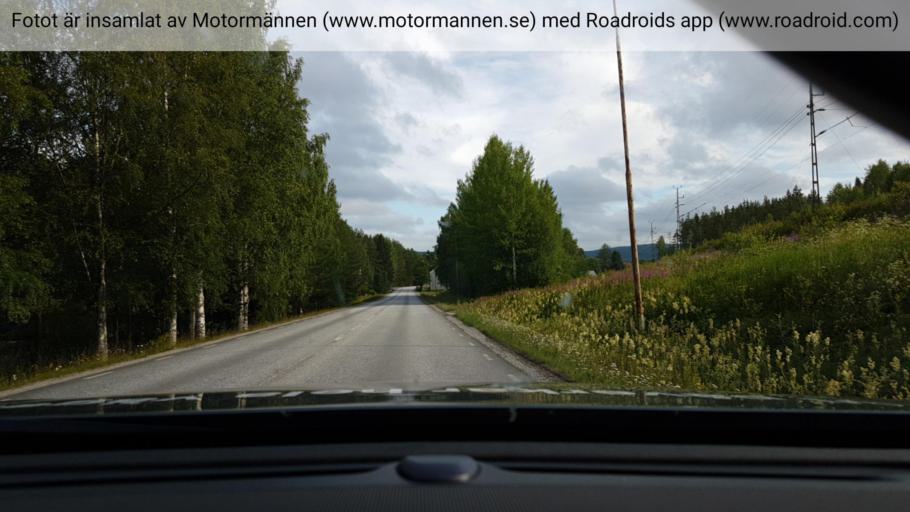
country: SE
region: Vaesterbotten
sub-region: Vindelns Kommun
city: Vindeln
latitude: 64.2221
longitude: 19.7071
